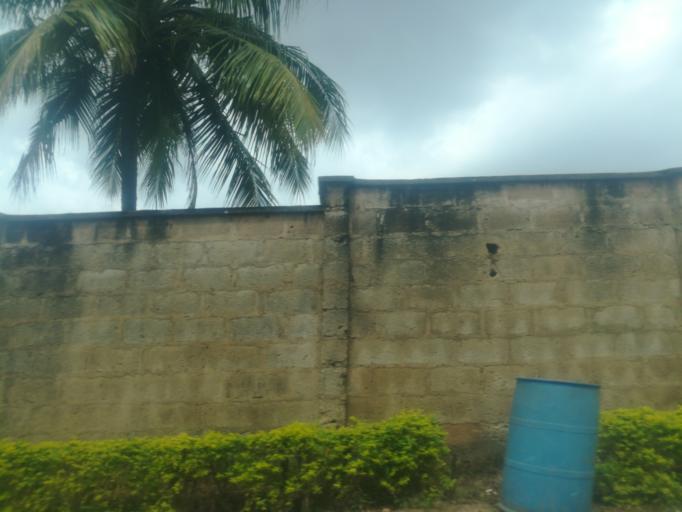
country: NG
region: Oyo
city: Ibadan
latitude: 7.4060
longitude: 3.9297
